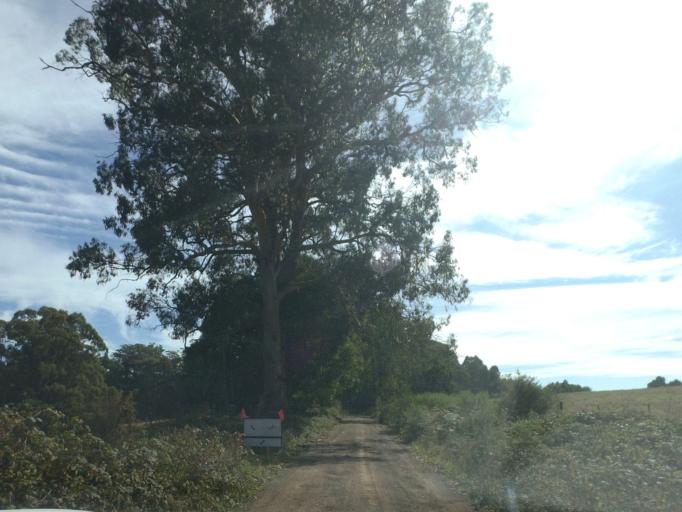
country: AU
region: Victoria
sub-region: Moorabool
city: Bacchus Marsh
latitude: -37.4161
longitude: 144.2496
